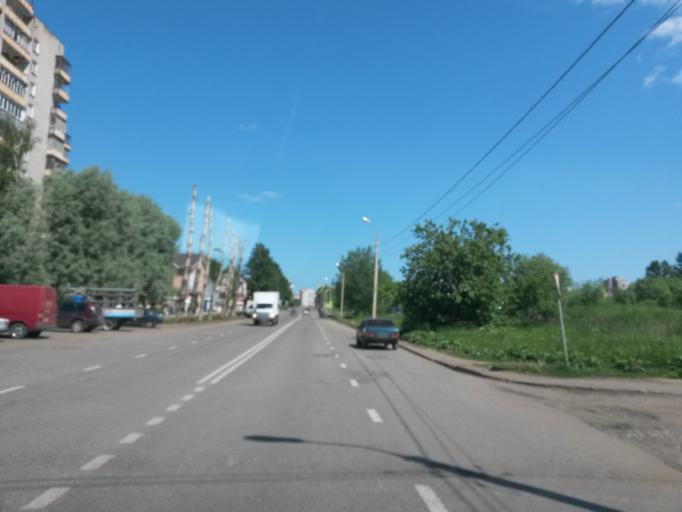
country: RU
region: Jaroslavl
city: Yaroslavl
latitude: 57.6870
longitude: 39.7678
